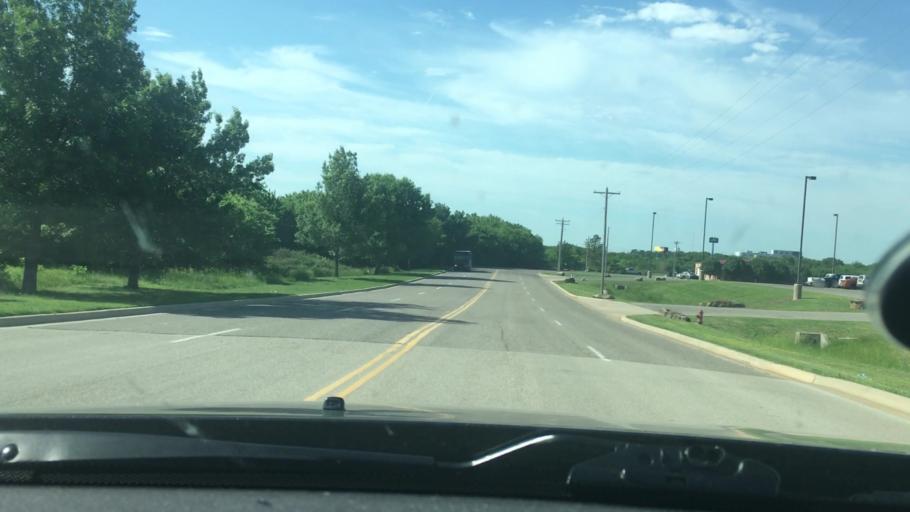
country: US
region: Oklahoma
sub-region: Carter County
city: Ardmore
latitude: 34.1957
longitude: -97.1672
